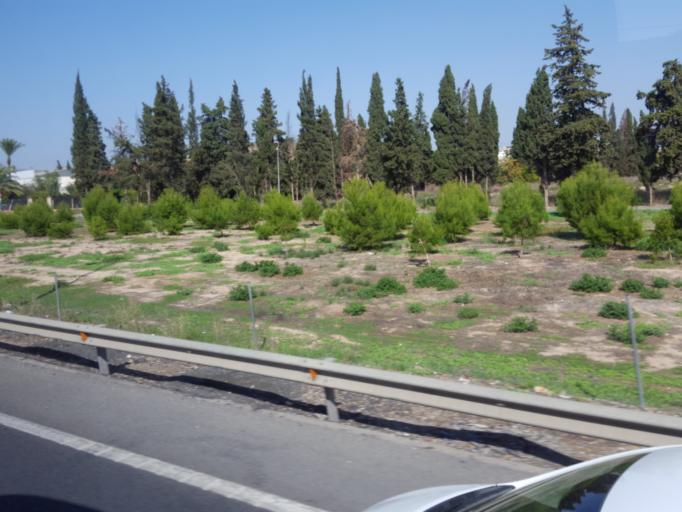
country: ES
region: Murcia
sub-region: Murcia
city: Murcia
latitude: 38.0025
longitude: -1.1623
